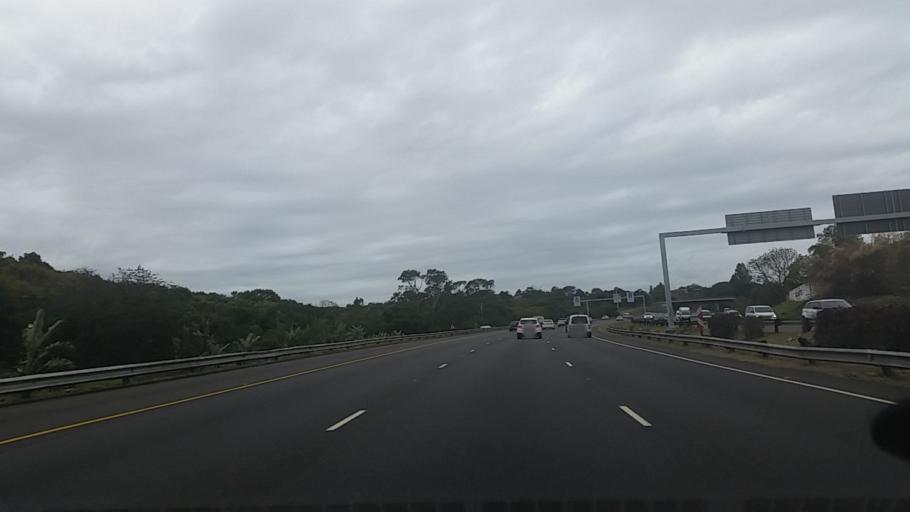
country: ZA
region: KwaZulu-Natal
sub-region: eThekwini Metropolitan Municipality
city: Berea
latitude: -29.8393
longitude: 30.9621
